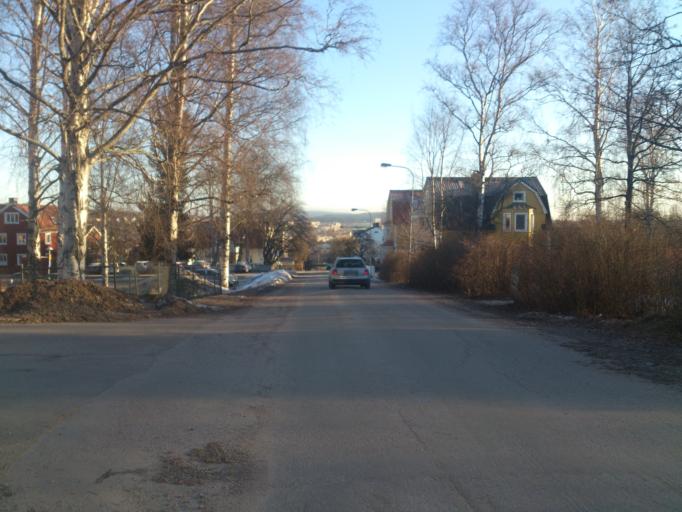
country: SE
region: Vaesternorrland
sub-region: Sundsvalls Kommun
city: Sundsvall
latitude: 62.3814
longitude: 17.3163
